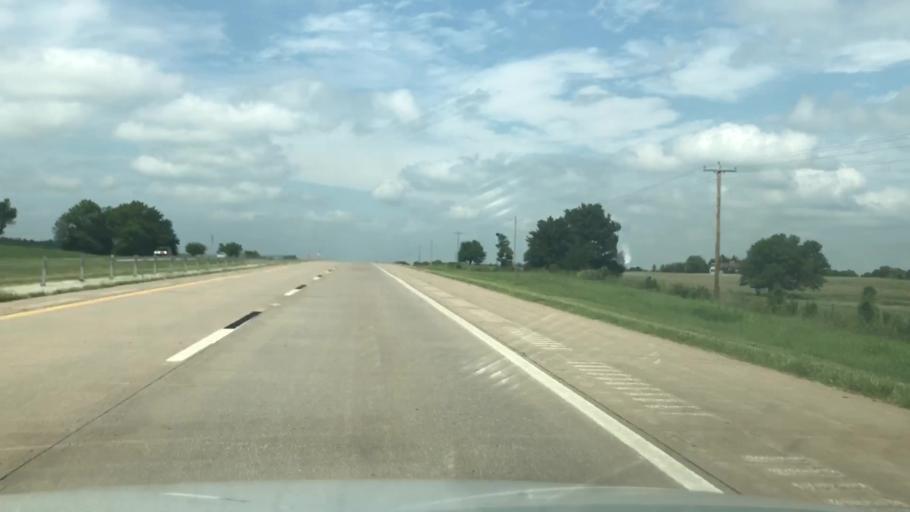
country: US
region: Oklahoma
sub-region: Osage County
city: Skiatook
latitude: 36.4429
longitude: -95.9205
